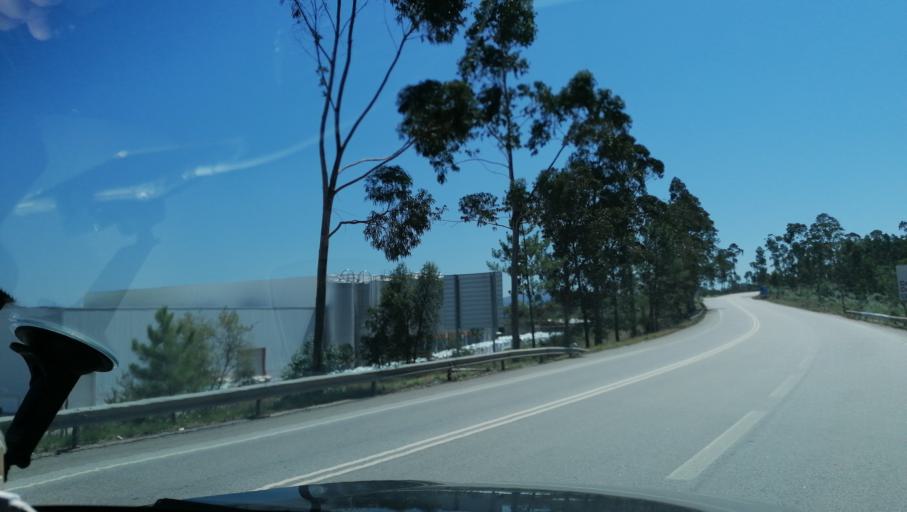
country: PT
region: Aveiro
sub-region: Mealhada
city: Mealhada
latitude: 40.3506
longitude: -8.4518
